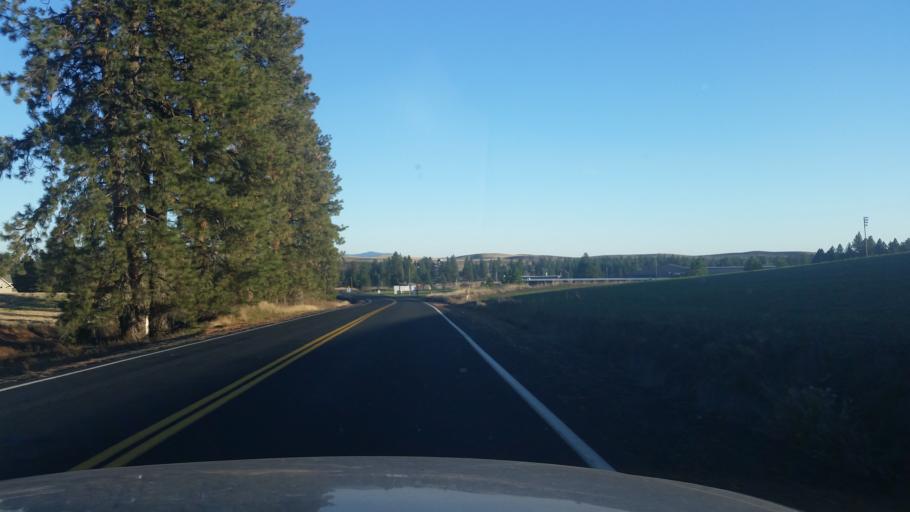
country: US
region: Washington
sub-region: Spokane County
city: Cheney
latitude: 47.3863
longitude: -117.3213
